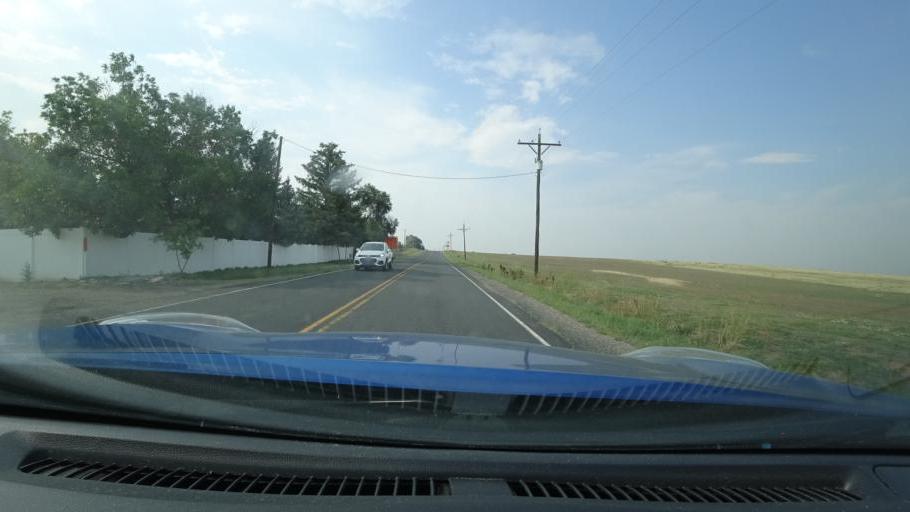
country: US
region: Colorado
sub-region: Adams County
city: Aurora
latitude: 39.7301
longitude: -104.7349
